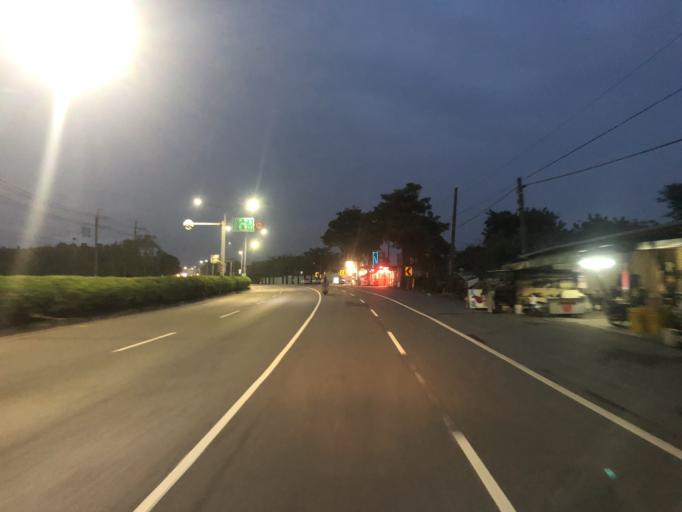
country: TW
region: Taiwan
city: Yujing
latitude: 23.1655
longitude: 120.3408
